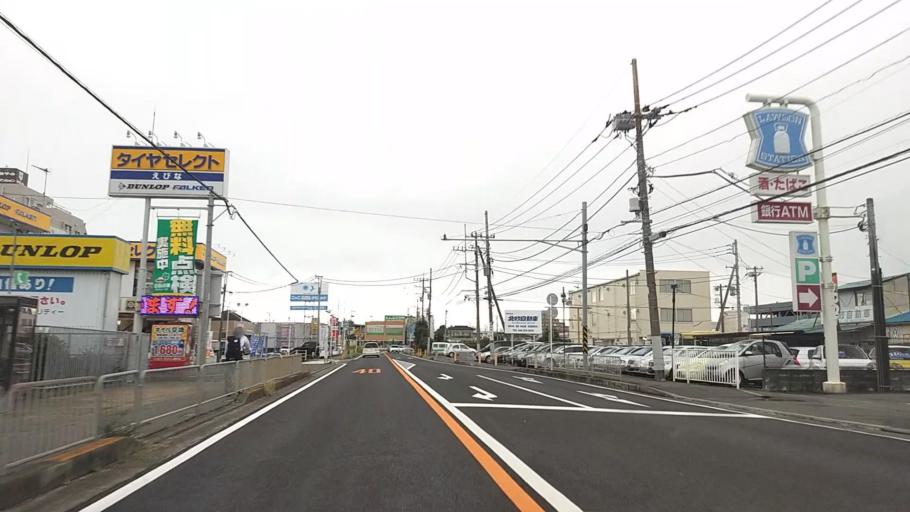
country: JP
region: Kanagawa
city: Atsugi
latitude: 35.4490
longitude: 139.3778
